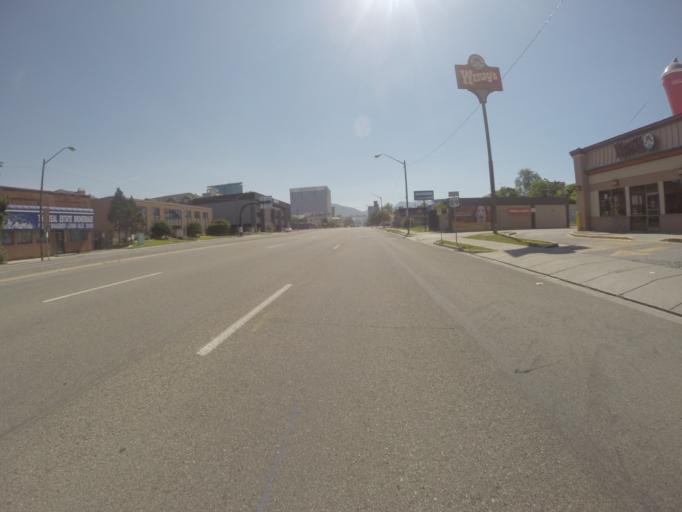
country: US
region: Utah
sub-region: Salt Lake County
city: Salt Lake City
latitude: 40.7606
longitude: -111.8988
